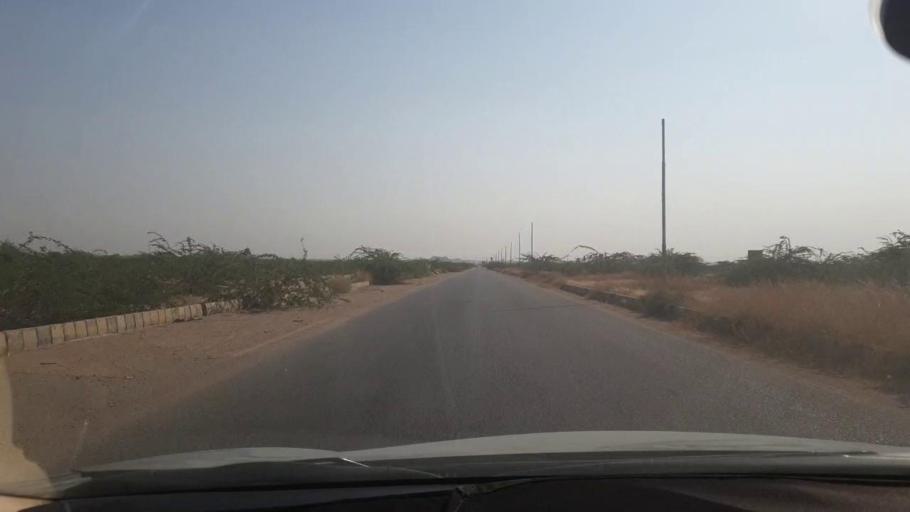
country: PK
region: Sindh
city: Malir Cantonment
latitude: 25.0661
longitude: 67.1389
